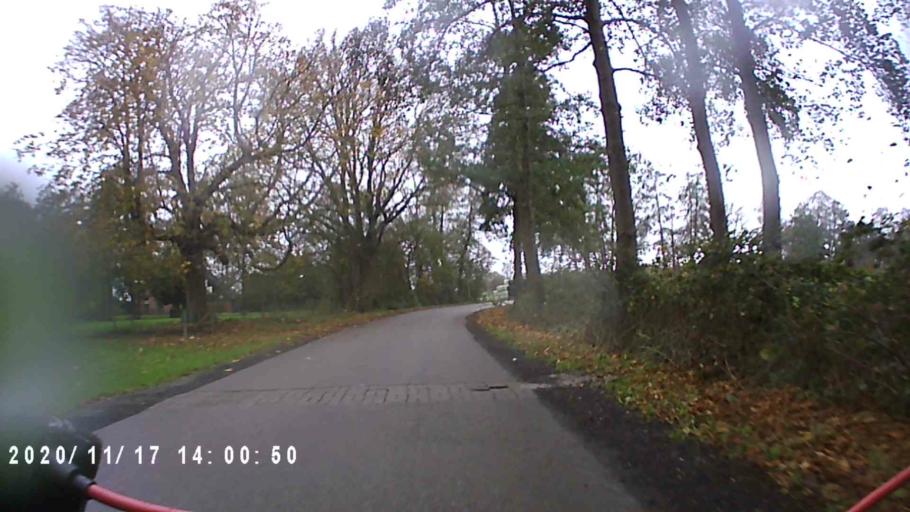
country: NL
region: Groningen
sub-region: Gemeente Zuidhorn
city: Grijpskerk
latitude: 53.2274
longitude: 6.3416
